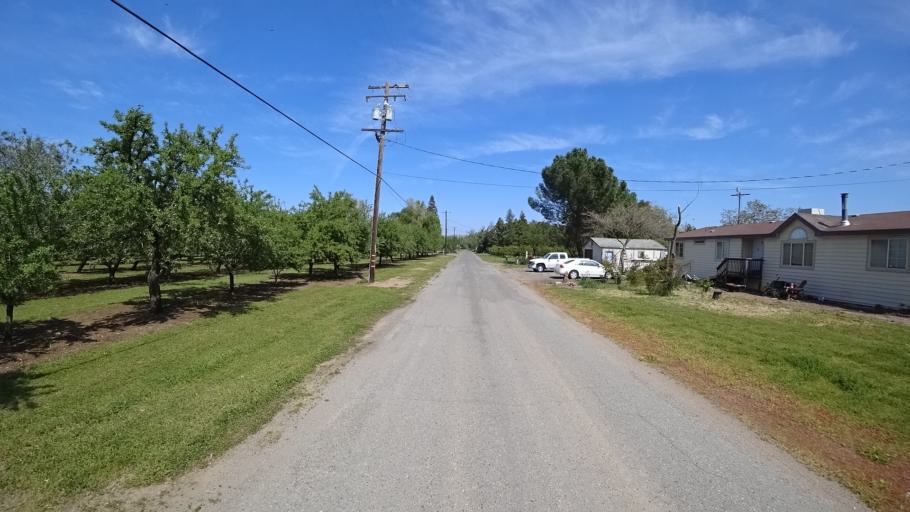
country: US
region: California
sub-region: Glenn County
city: Hamilton City
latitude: 39.8008
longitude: -122.0571
